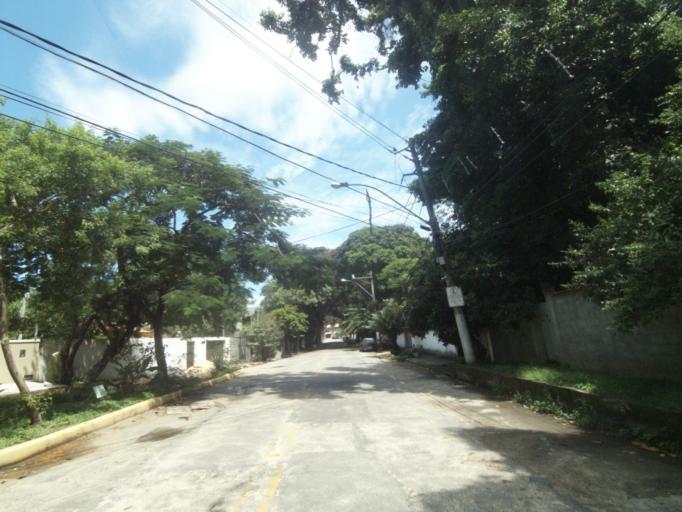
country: BR
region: Rio de Janeiro
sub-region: Niteroi
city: Niteroi
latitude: -22.9727
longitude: -43.0370
